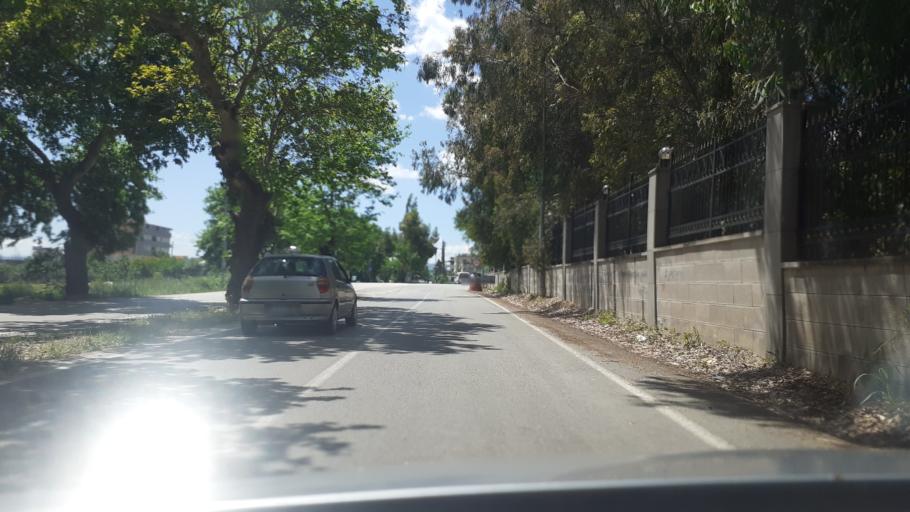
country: TR
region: Hatay
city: Anayazi
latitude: 36.3223
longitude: 36.1978
